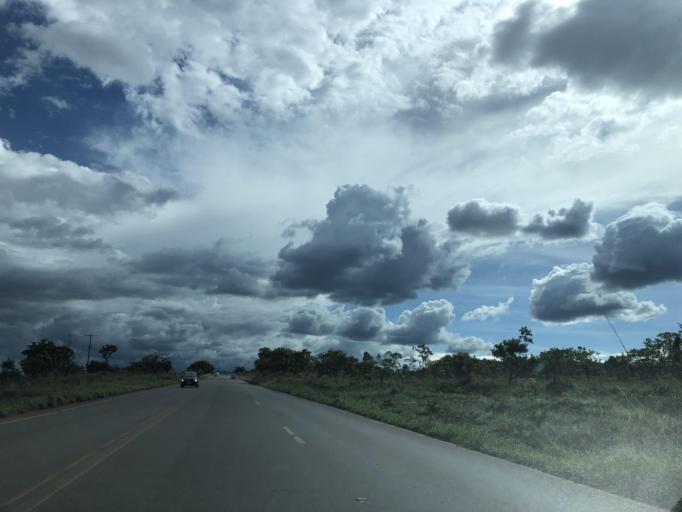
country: BR
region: Goias
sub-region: Luziania
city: Luziania
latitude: -16.0093
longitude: -48.1358
